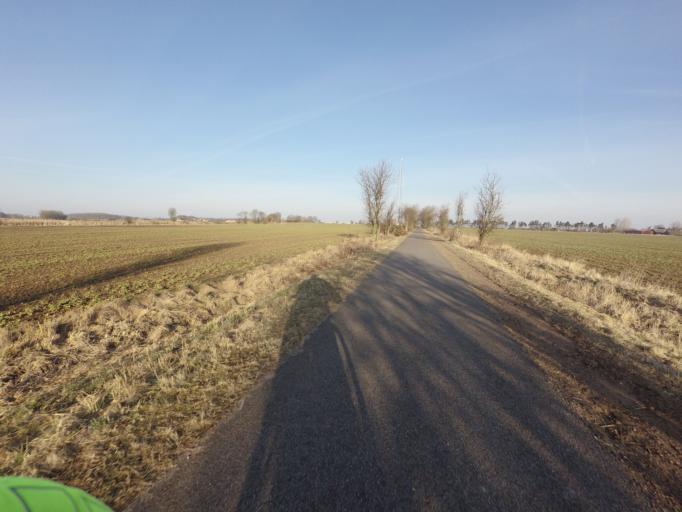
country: SE
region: Skane
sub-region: Hoganas Kommun
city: Hoganas
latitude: 56.1913
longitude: 12.6161
